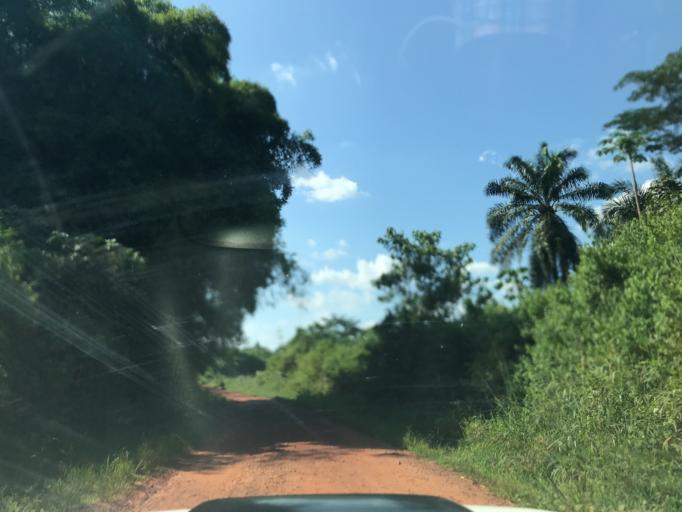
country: CD
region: Eastern Province
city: Kisangani
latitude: 1.2753
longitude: 25.2782
